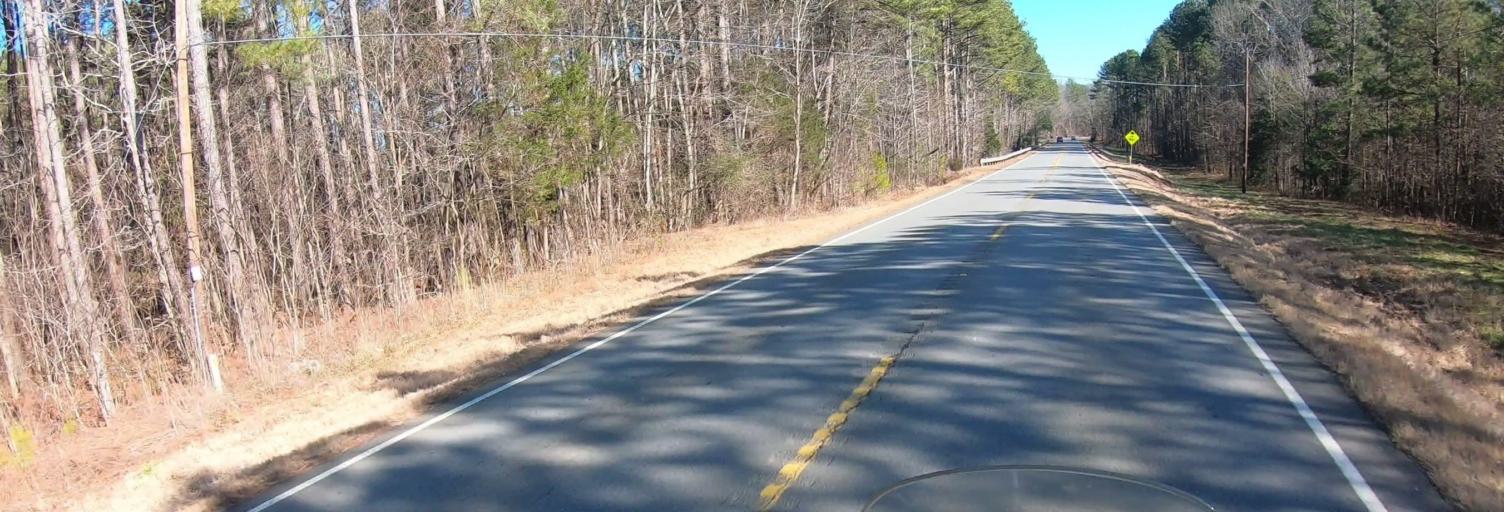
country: US
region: Georgia
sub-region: Murray County
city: Chatsworth
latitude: 34.5915
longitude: -84.6890
